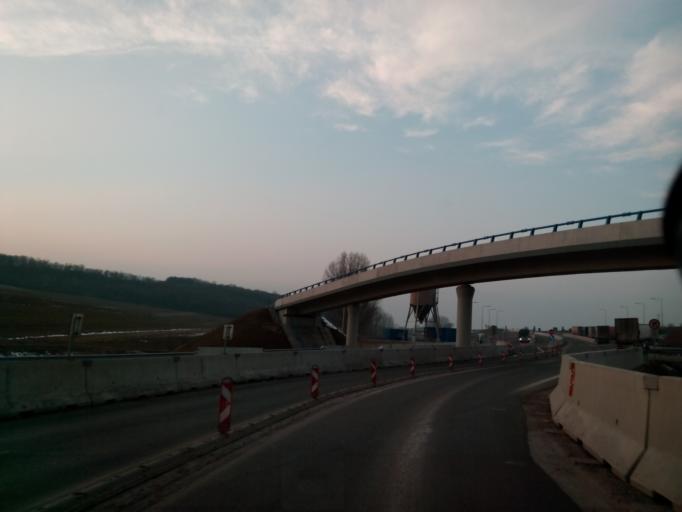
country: HU
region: Borsod-Abauj-Zemplen
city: Gonc
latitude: 48.5321
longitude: 21.2526
